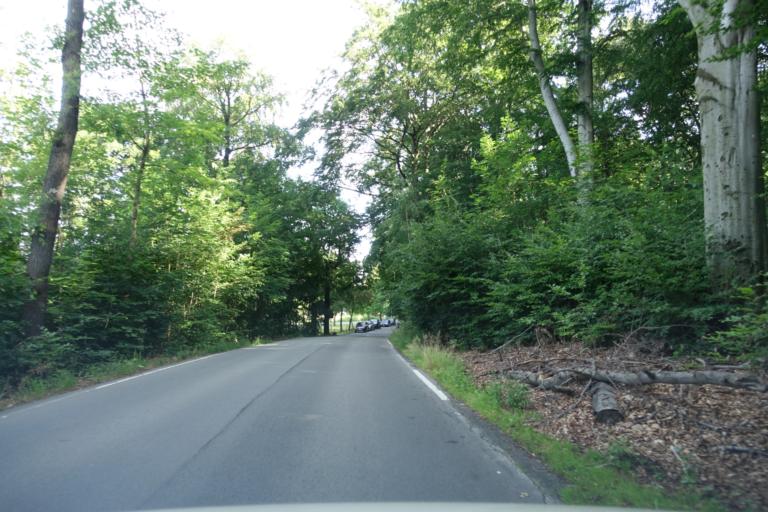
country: DE
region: Saxony
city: Hilbersdorf
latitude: 50.8524
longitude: 12.9588
